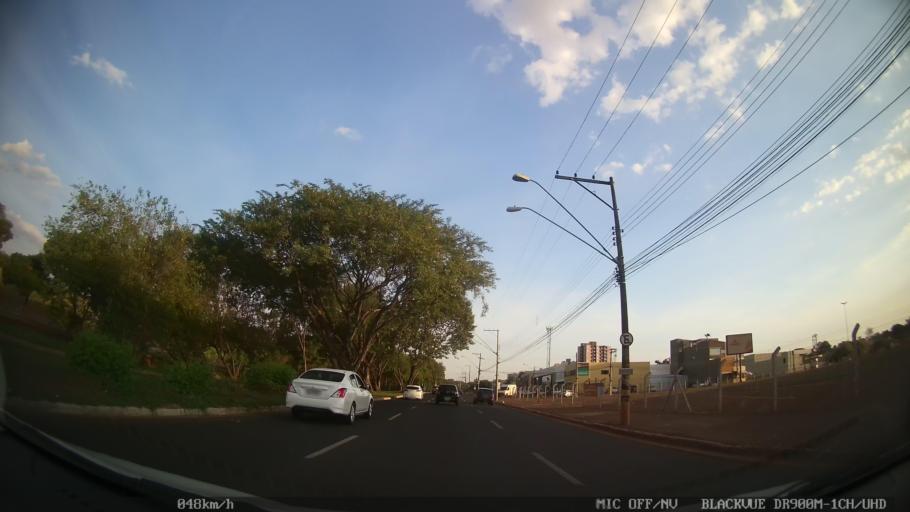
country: BR
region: Sao Paulo
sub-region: Ribeirao Preto
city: Ribeirao Preto
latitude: -21.1542
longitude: -47.8101
